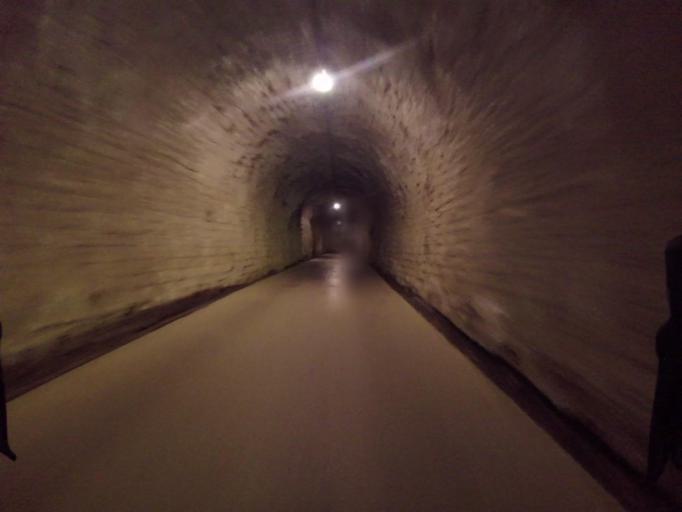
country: ES
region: Basque Country
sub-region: Provincia de Guipuzcoa
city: Andoain
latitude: 43.2128
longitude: -2.0138
